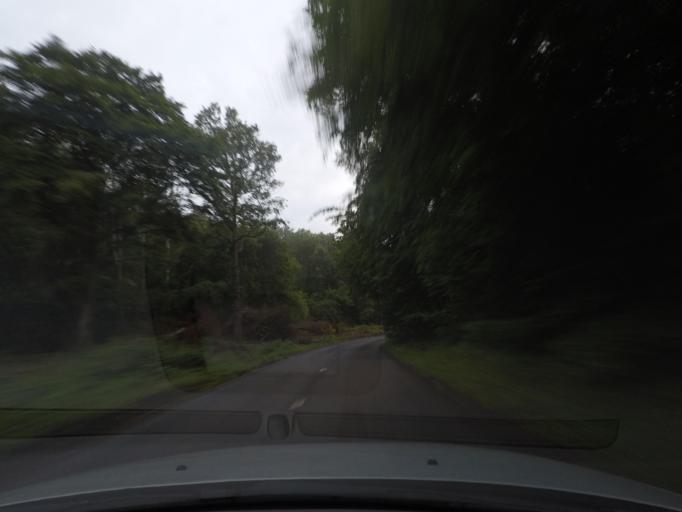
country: FR
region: Haute-Normandie
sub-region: Departement de la Seine-Maritime
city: Fontaine-le-Bourg
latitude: 49.5521
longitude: 1.1212
